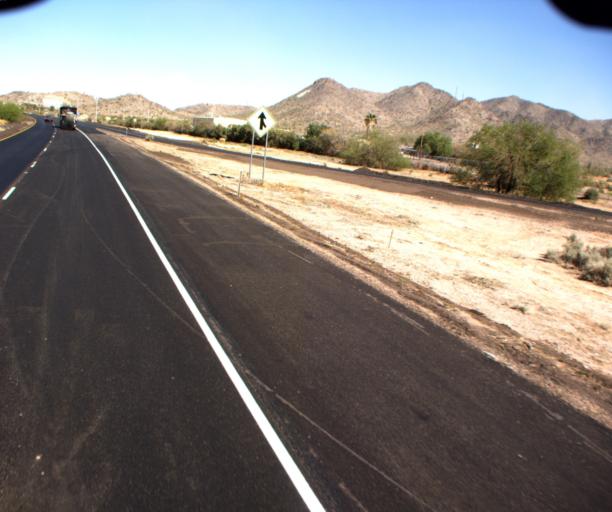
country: US
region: Arizona
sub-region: Pinal County
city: Casa Grande
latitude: 32.8287
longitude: -111.7384
